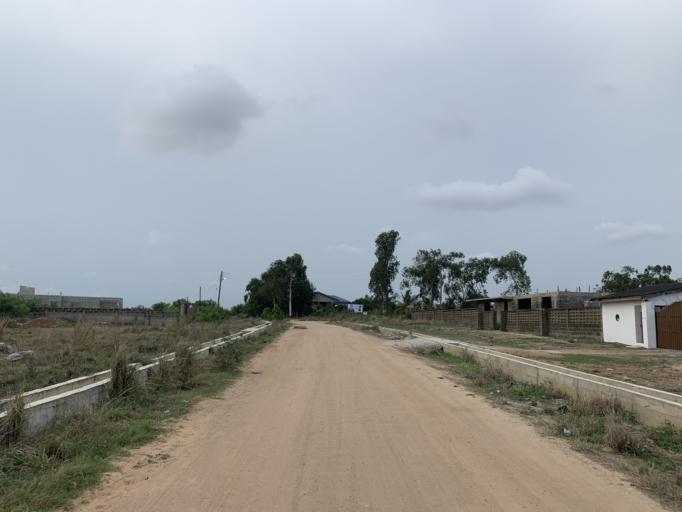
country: GH
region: Central
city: Winneba
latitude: 5.3869
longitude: -0.6336
